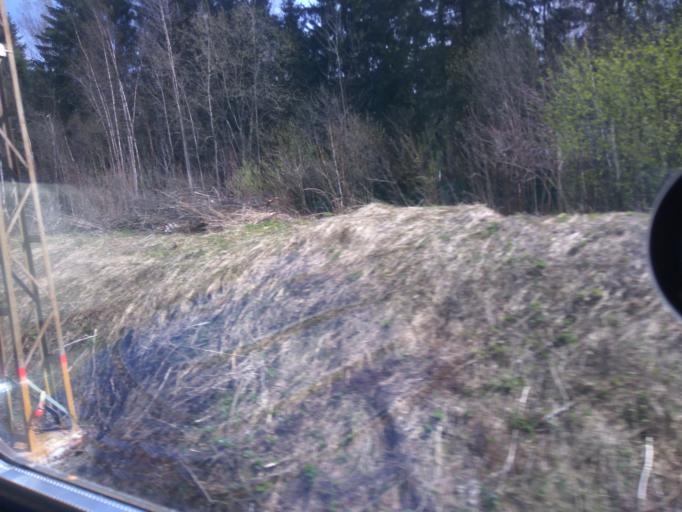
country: RU
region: Moskovskaya
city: Nekrasovskiy
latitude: 56.1149
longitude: 37.5112
